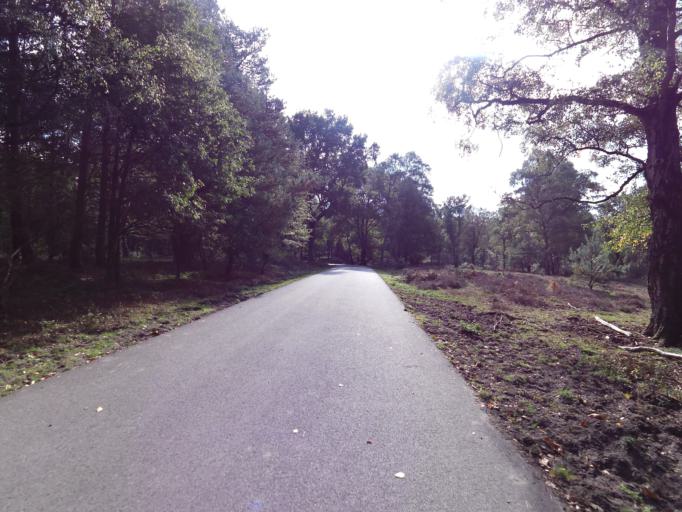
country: NL
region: Gelderland
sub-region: Gemeente Rheden
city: Rheden
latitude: 52.0186
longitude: 6.0124
